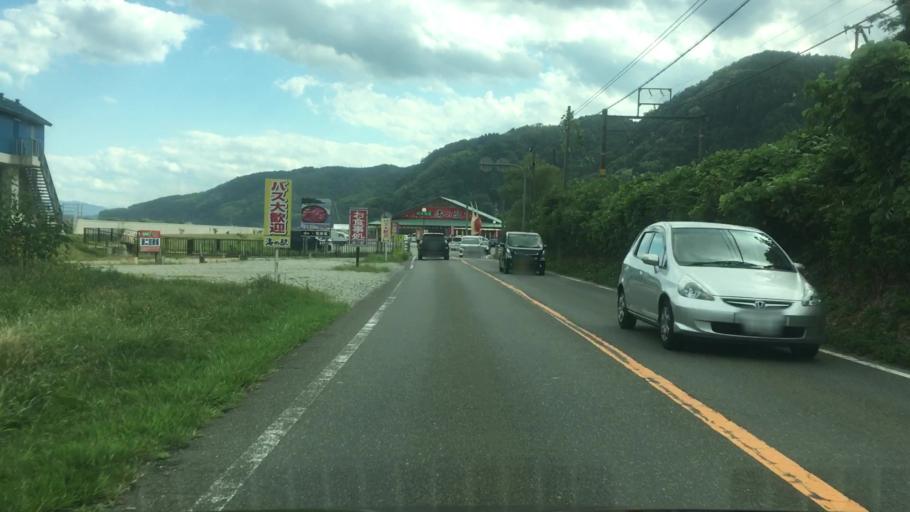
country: JP
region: Hyogo
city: Toyooka
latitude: 35.5950
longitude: 134.8012
